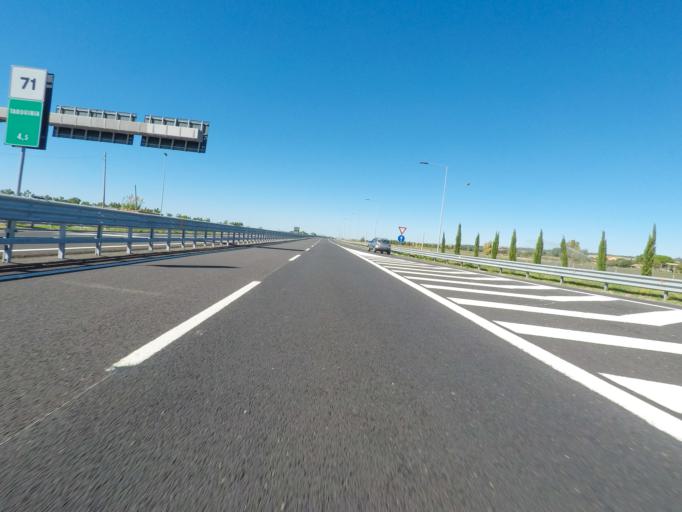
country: IT
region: Latium
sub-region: Provincia di Viterbo
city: Tarquinia
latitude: 42.2126
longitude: 11.7790
